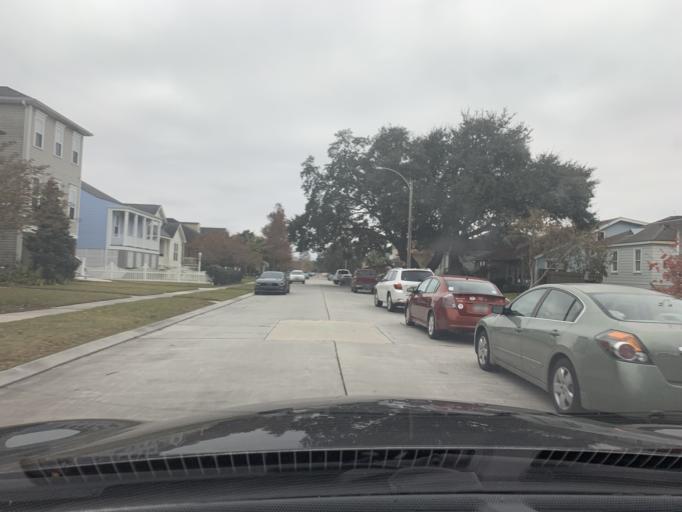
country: US
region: Louisiana
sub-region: Jefferson Parish
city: Metairie
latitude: 30.0104
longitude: -90.1108
